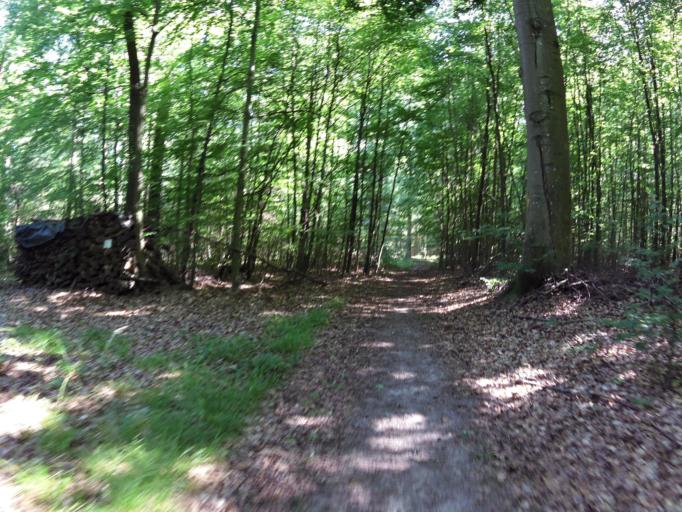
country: DE
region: Bavaria
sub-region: Regierungsbezirk Unterfranken
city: Margetshochheim
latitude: 49.8566
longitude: 9.8766
